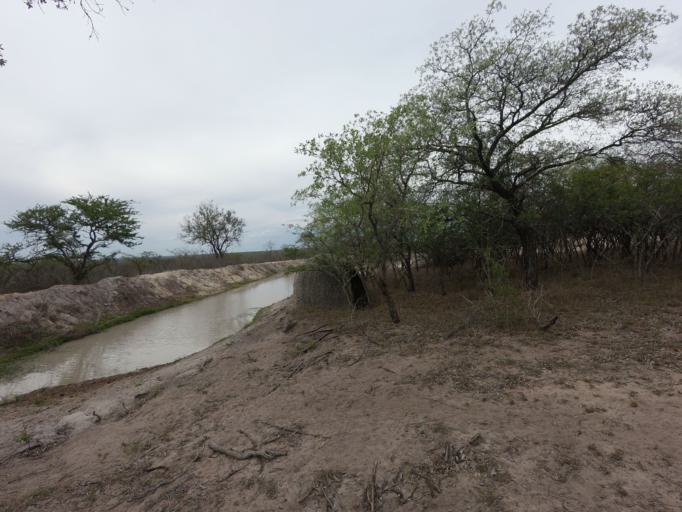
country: ZA
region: Limpopo
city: Thulamahashi
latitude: -24.5282
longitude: 31.1134
